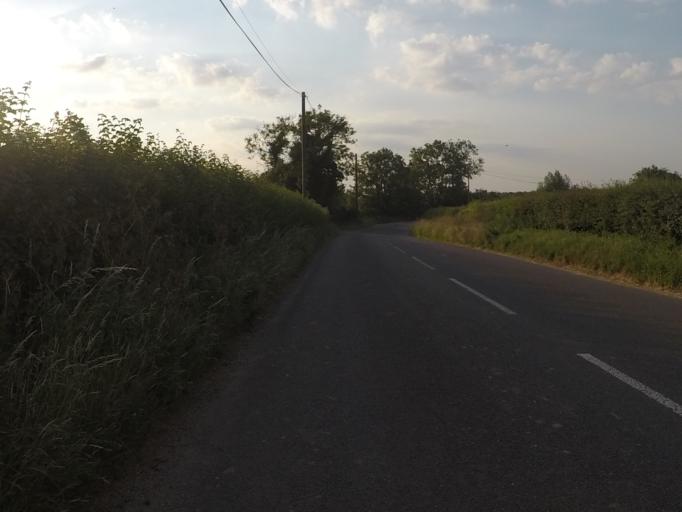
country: GB
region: England
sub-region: Oxfordshire
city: Charlbury
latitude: 51.8843
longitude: -1.4899
